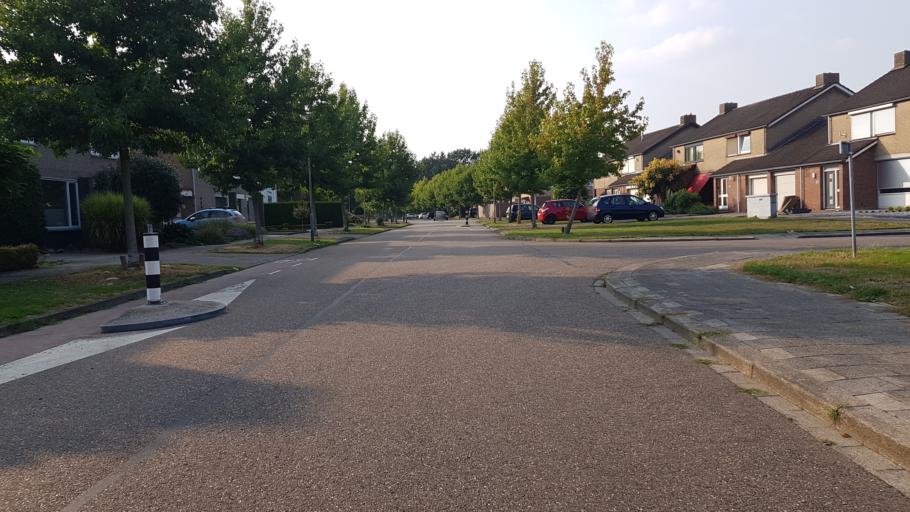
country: NL
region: Limburg
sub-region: Gemeente Beek
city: Beek
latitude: 50.9505
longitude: 5.8110
